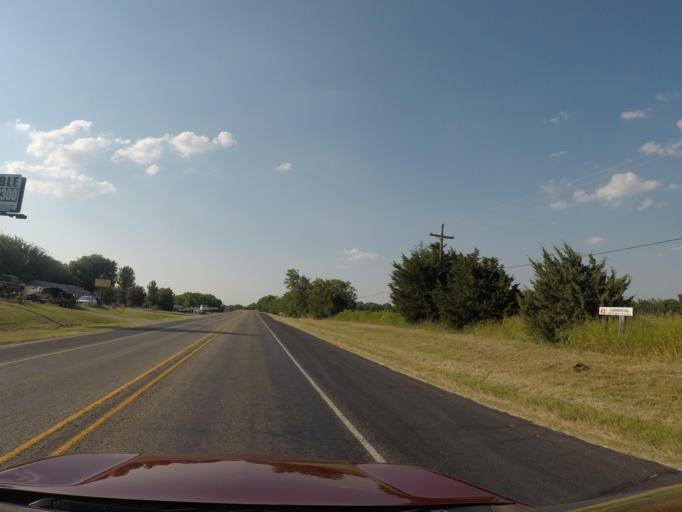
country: US
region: Texas
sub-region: Grayson County
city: Denison
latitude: 33.7972
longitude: -96.5563
